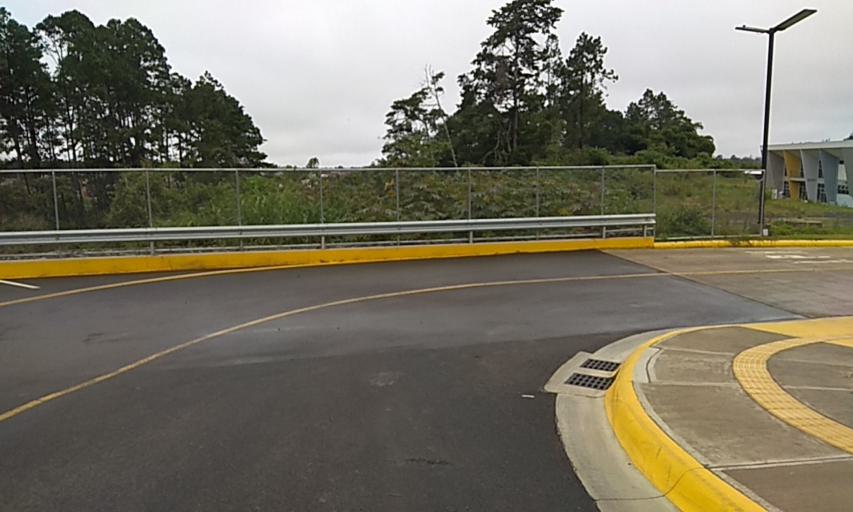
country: CR
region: Cartago
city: Cartago
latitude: 9.8545
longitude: -83.9065
